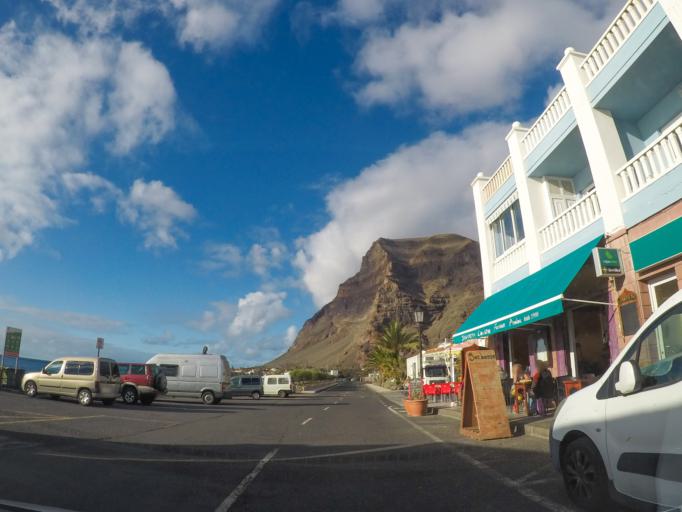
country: ES
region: Canary Islands
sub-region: Provincia de Santa Cruz de Tenerife
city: Alajero
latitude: 28.0883
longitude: -17.3391
